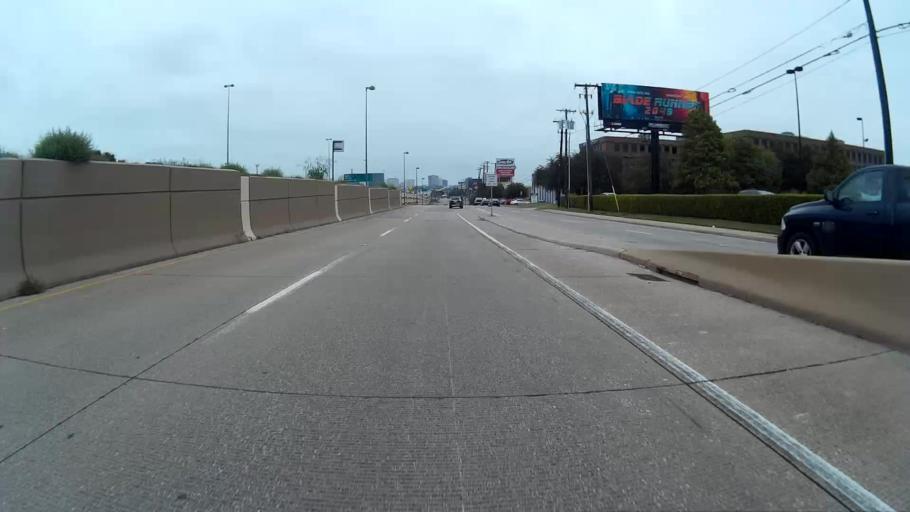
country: US
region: Texas
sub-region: Dallas County
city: University Park
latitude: 32.8954
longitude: -96.7688
